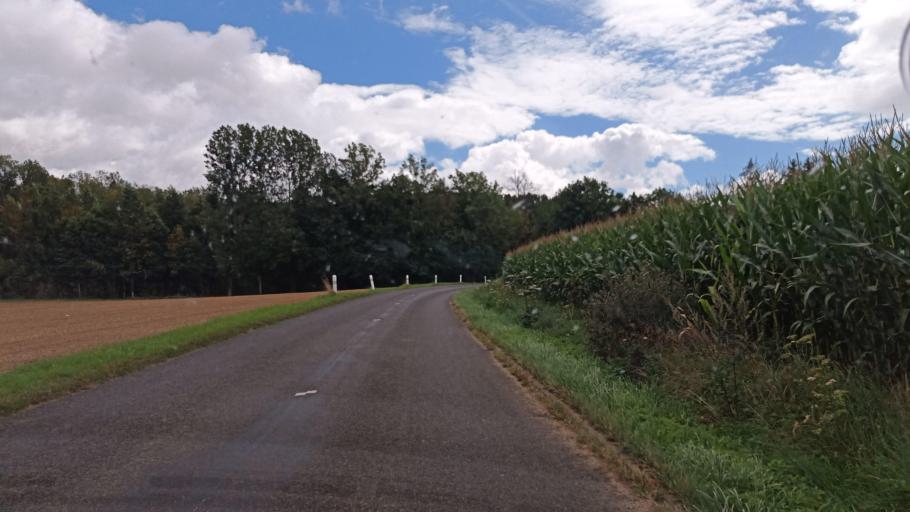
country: FR
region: Ile-de-France
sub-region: Departement de Seine-et-Marne
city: Voulx
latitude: 48.2639
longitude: 3.0108
